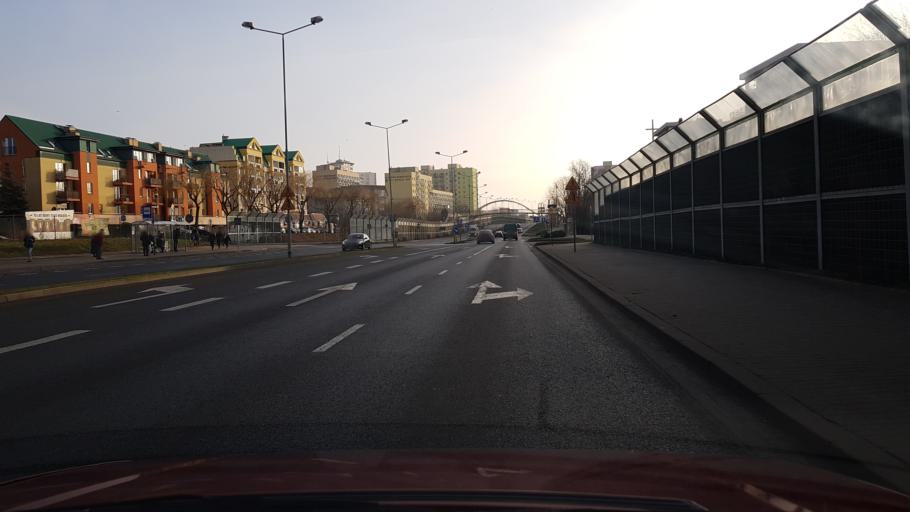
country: PL
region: West Pomeranian Voivodeship
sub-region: Szczecin
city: Szczecin
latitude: 53.4543
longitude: 14.5524
